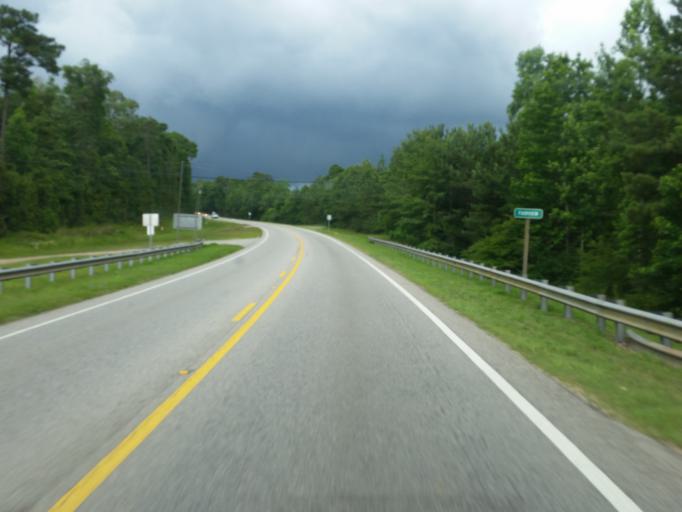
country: US
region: Mississippi
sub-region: Jackson County
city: Hurley
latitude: 30.7999
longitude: -88.3313
